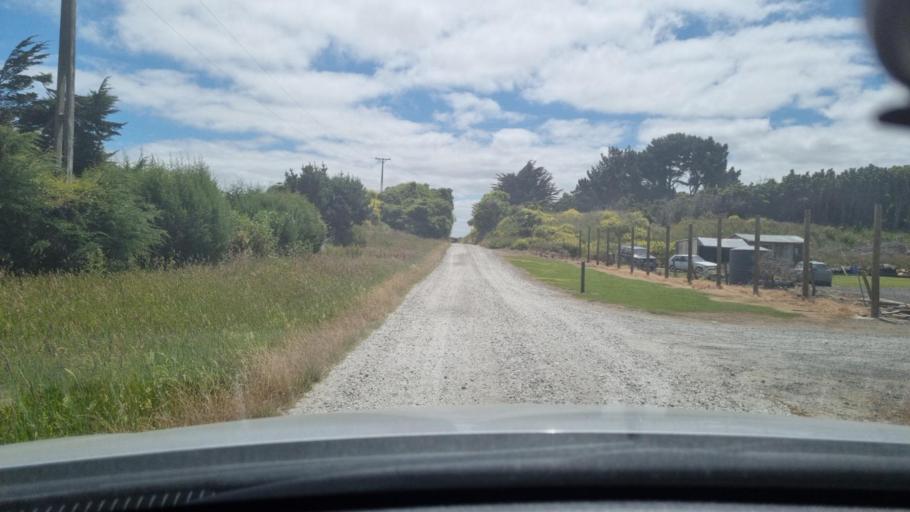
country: NZ
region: Southland
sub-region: Invercargill City
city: Invercargill
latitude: -46.4546
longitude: 168.2813
